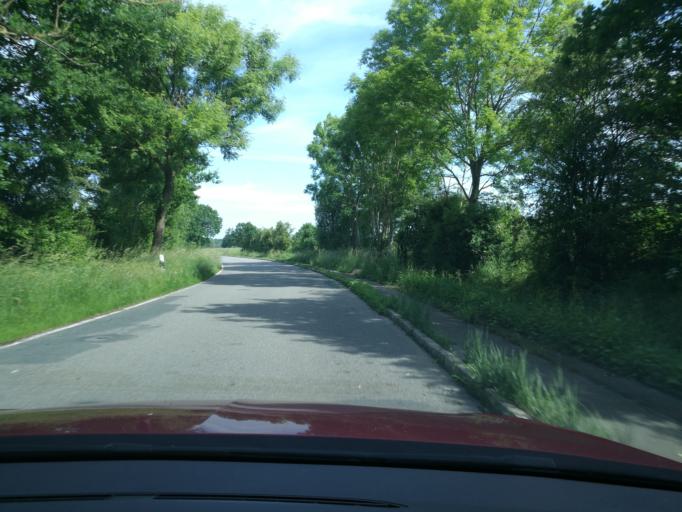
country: DE
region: Schleswig-Holstein
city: Lasbek
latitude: 53.7364
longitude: 10.3500
